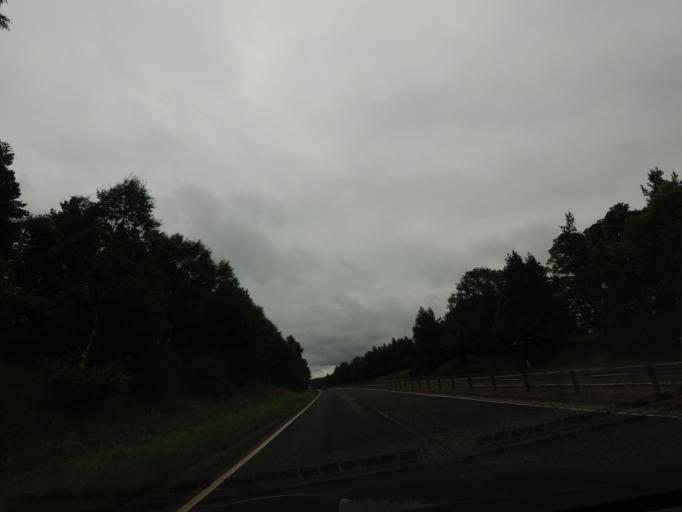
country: GB
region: Scotland
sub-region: Highland
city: Inverness
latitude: 57.4369
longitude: -4.1391
